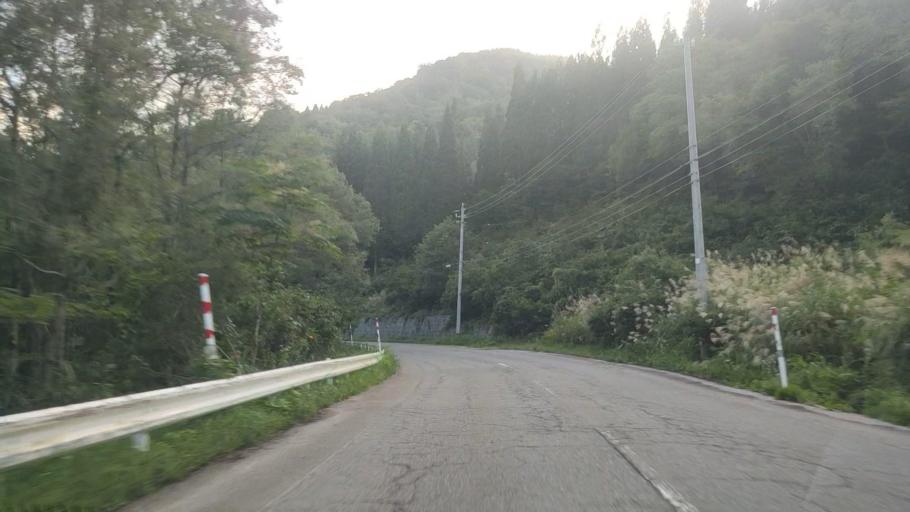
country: JP
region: Toyama
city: Yatsuomachi-higashikumisaka
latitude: 36.4833
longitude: 137.0486
